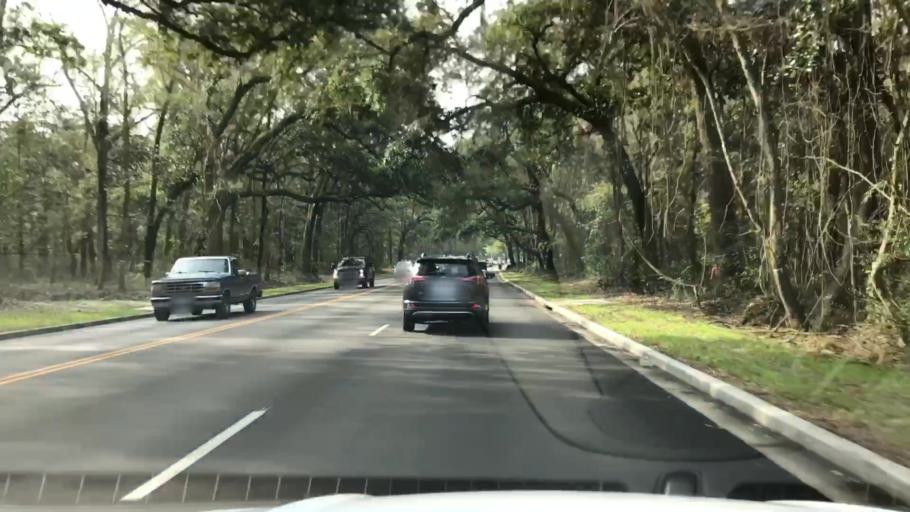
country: US
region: South Carolina
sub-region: Charleston County
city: Shell Point
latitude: 32.7464
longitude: -80.0352
